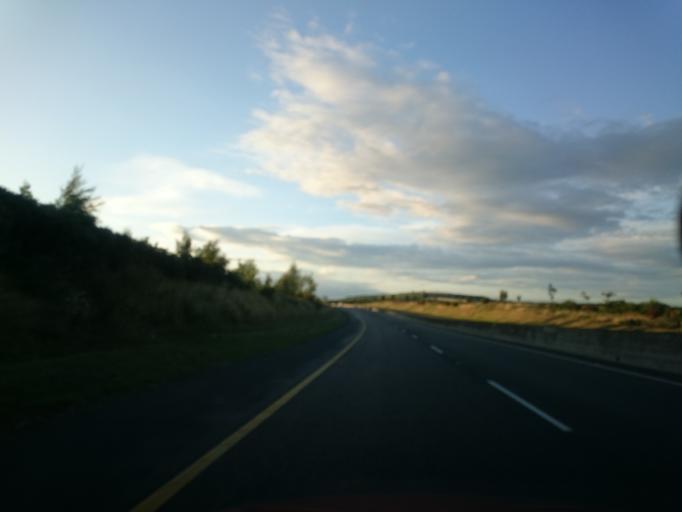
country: IE
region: Leinster
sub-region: Loch Garman
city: Gorey
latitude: 52.6752
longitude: -6.2577
